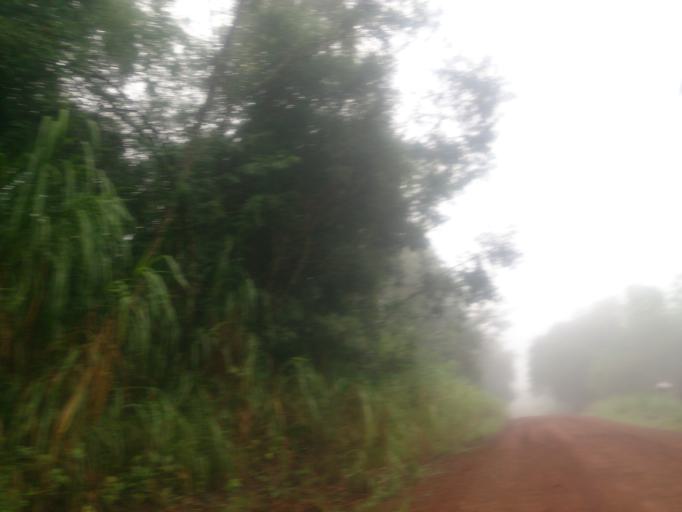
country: AR
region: Misiones
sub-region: Departamento de Obera
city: Obera
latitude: -27.4662
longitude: -55.1062
